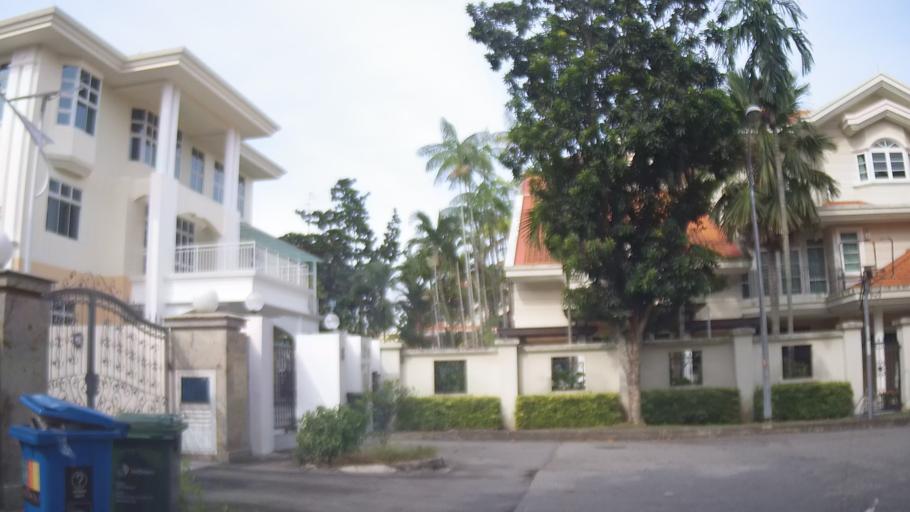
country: MY
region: Johor
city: Johor Bahru
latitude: 1.4270
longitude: 103.7794
